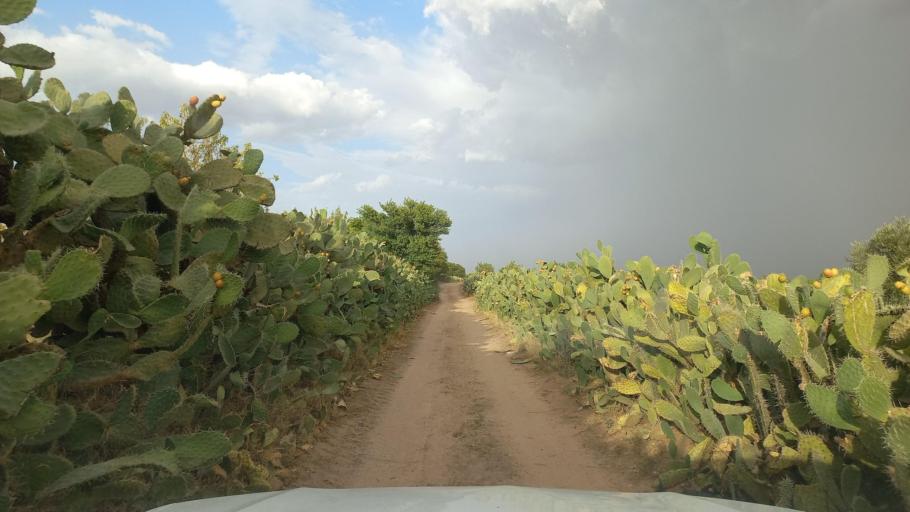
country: TN
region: Al Qasrayn
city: Kasserine
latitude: 35.2816
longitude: 9.0570
